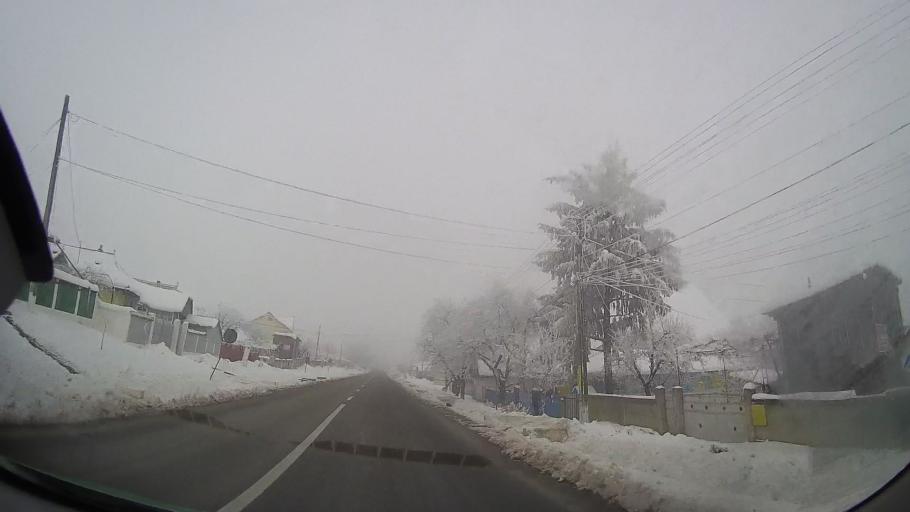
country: RO
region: Iasi
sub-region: Comuna Mircesti
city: Mircesti
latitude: 47.0963
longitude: 26.8194
